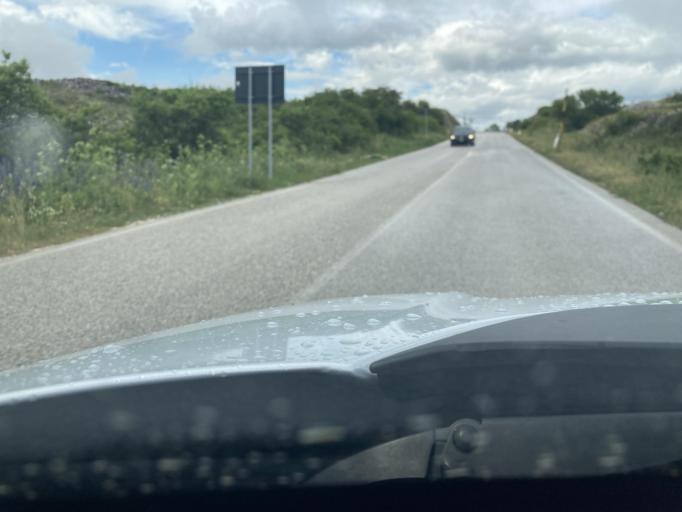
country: IT
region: Abruzzo
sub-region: Provincia dell' Aquila
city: Rocca di Mezzo
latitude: 42.2301
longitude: 13.5338
